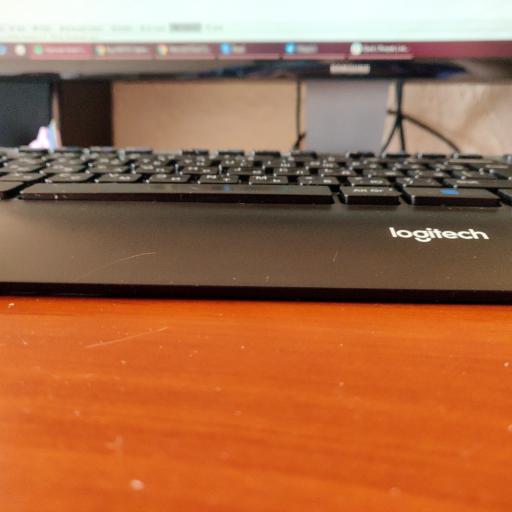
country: FI
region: Satakunta
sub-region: Pohjois-Satakunta
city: Kankaanpaeae
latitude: 61.7278
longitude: 22.3068
